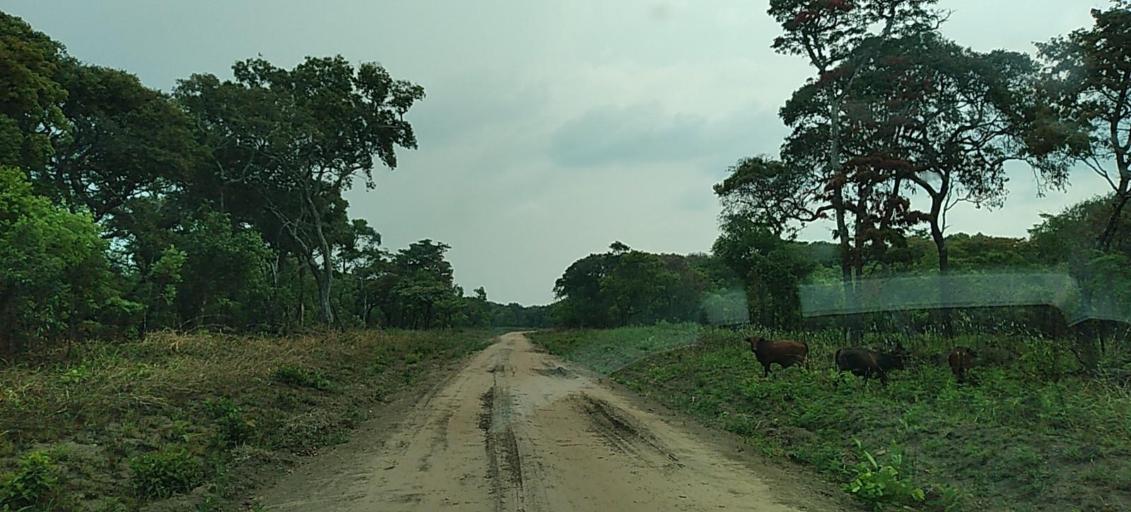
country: ZM
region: North-Western
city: Mwinilunga
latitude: -11.4087
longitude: 24.6201
